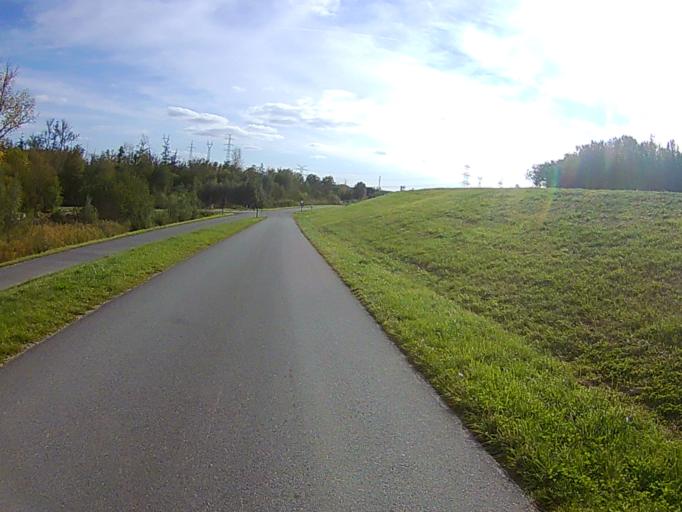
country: BE
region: Flanders
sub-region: Provincie Oost-Vlaanderen
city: Kruibeke
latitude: 51.1386
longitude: 4.3049
